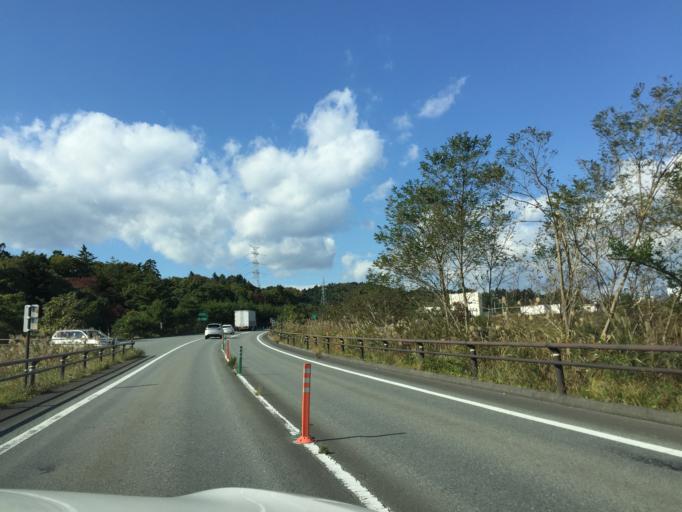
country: JP
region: Fukushima
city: Iwaki
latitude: 37.2339
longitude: 140.9875
